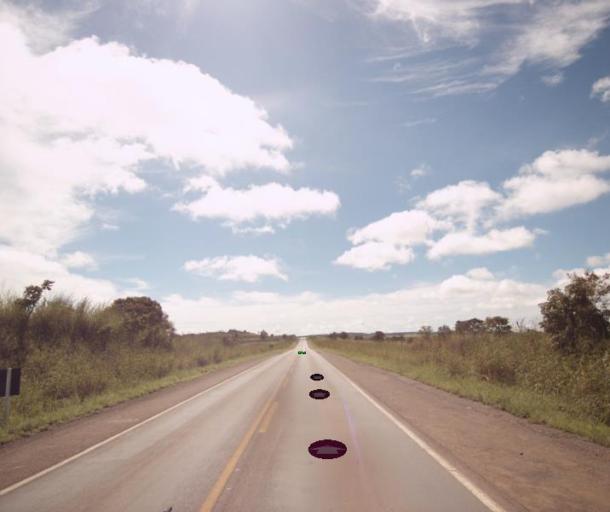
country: BR
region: Goias
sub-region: Padre Bernardo
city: Padre Bernardo
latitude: -15.2203
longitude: -48.5196
